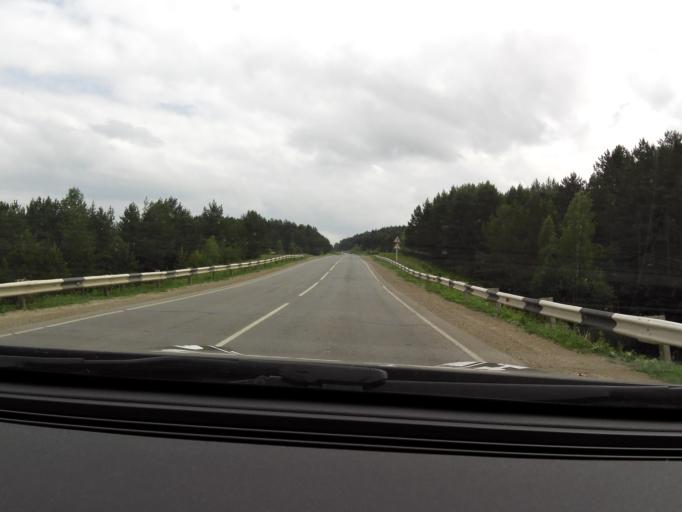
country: RU
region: Perm
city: Kungur
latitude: 57.4805
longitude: 56.7062
